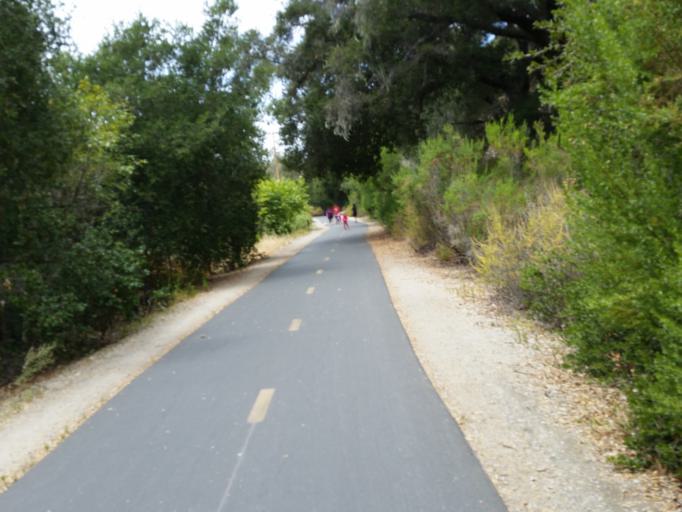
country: US
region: California
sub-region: San Luis Obispo County
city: Avila Beach
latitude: 35.1879
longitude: -120.7113
